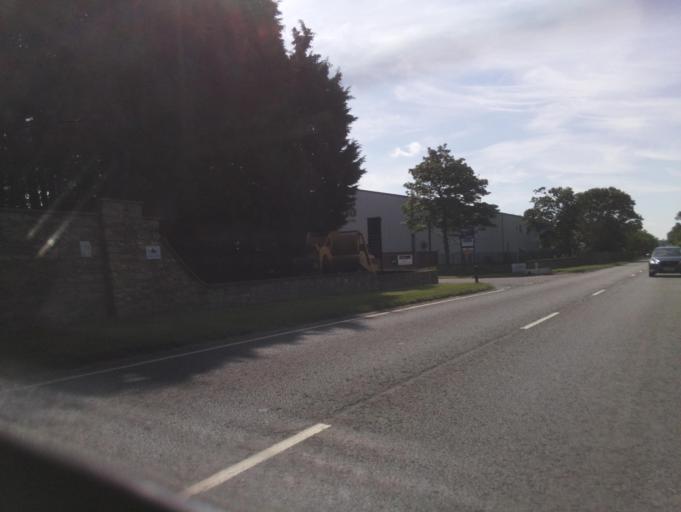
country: GB
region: England
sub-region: North Lincolnshire
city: Kirton in Lindsey
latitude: 53.3836
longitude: -0.5470
